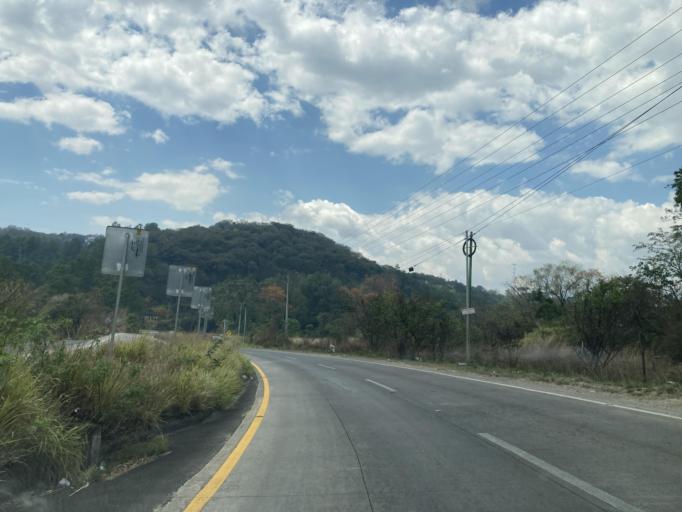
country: GT
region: Santa Rosa
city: Barberena
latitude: 14.3379
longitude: -90.4402
